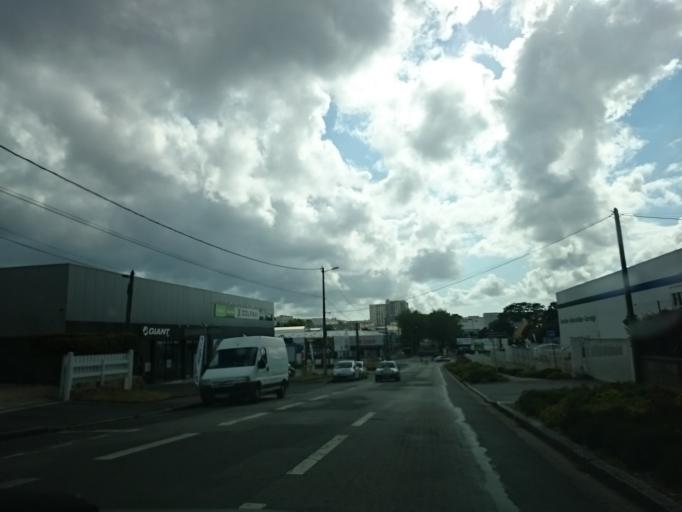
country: FR
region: Brittany
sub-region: Departement du Finistere
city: Brest
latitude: 48.4121
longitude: -4.4552
